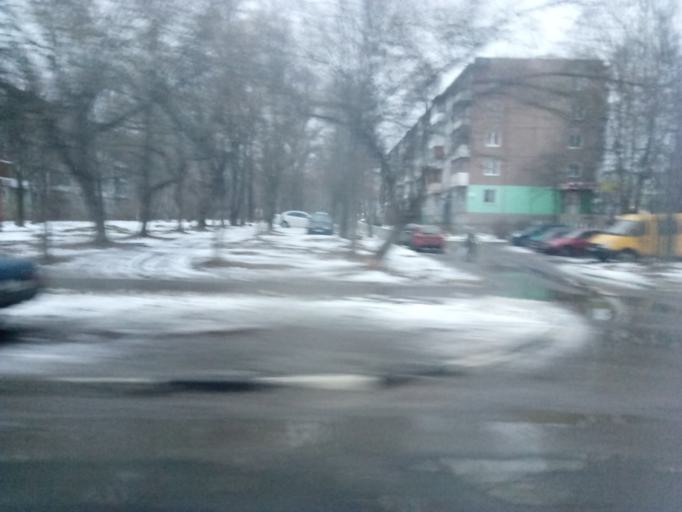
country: RU
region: Tula
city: Kosaya Gora
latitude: 54.1935
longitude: 37.5349
